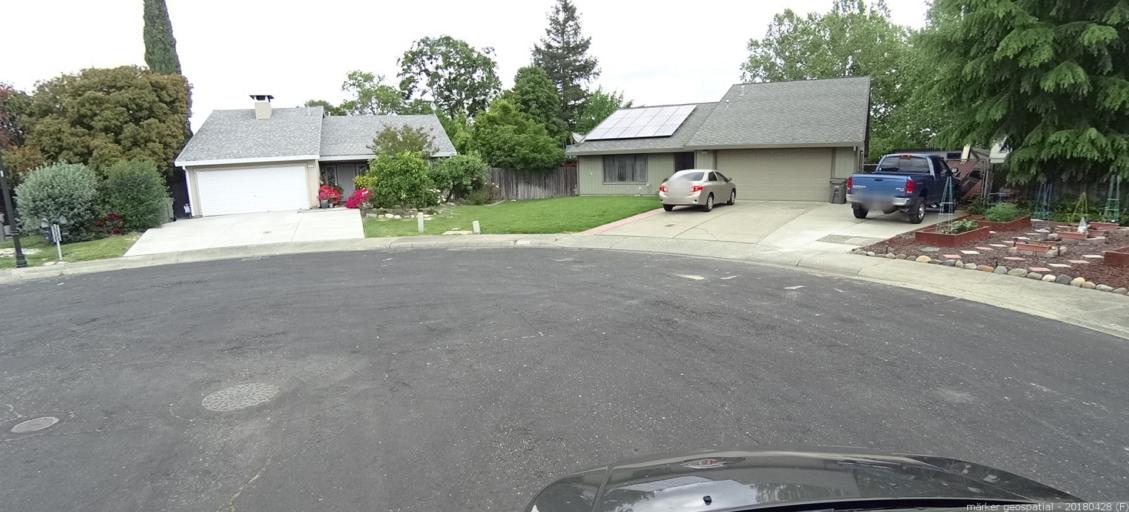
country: US
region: California
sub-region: Yolo County
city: West Sacramento
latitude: 38.5519
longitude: -121.5522
